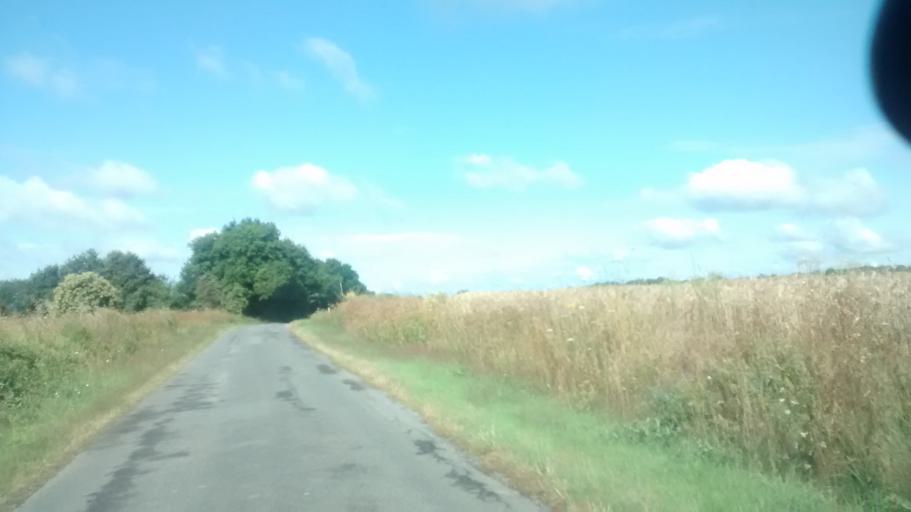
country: FR
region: Brittany
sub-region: Departement d'Ille-et-Vilaine
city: La Dominelais
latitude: 47.7842
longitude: -1.7098
